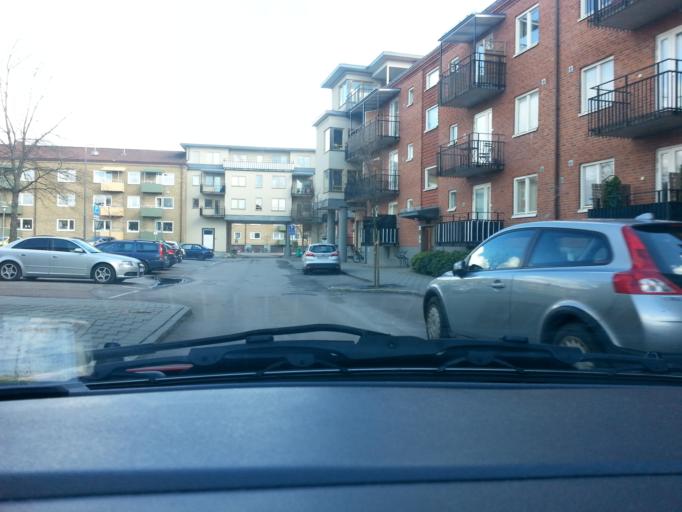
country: SE
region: Vaestra Goetaland
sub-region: Partille Kommun
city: Partille
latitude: 57.7391
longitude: 12.1089
